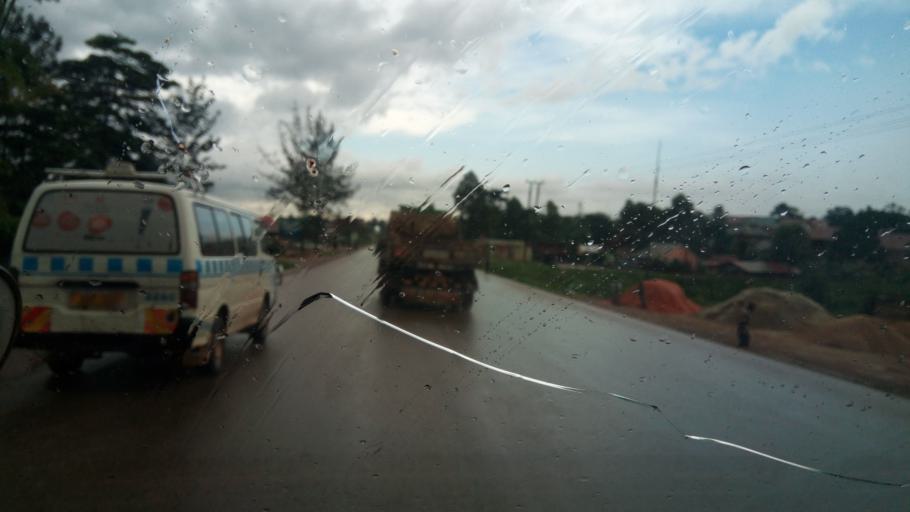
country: UG
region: Central Region
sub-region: Wakiso District
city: Wakiso
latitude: 0.3976
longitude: 32.4837
